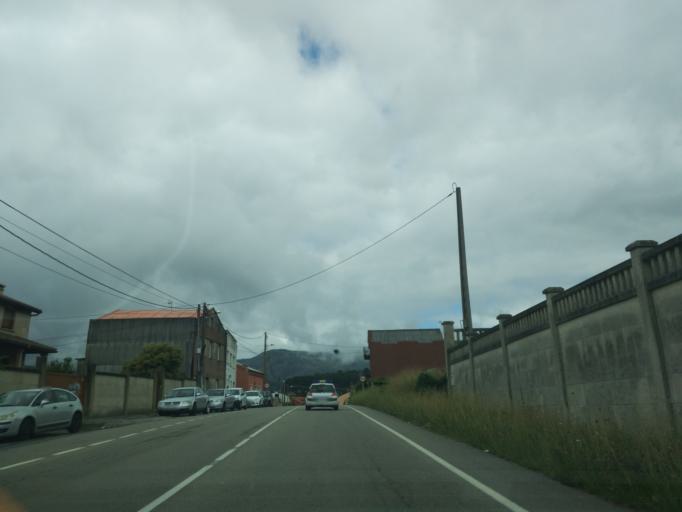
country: ES
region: Galicia
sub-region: Provincia da Coruna
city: Boiro
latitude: 42.6450
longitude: -8.8728
